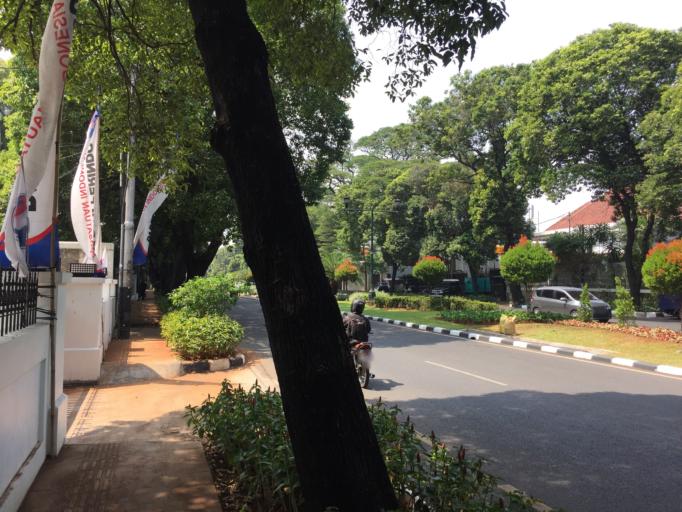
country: ID
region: Jakarta Raya
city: Jakarta
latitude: -6.2010
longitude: 106.8382
